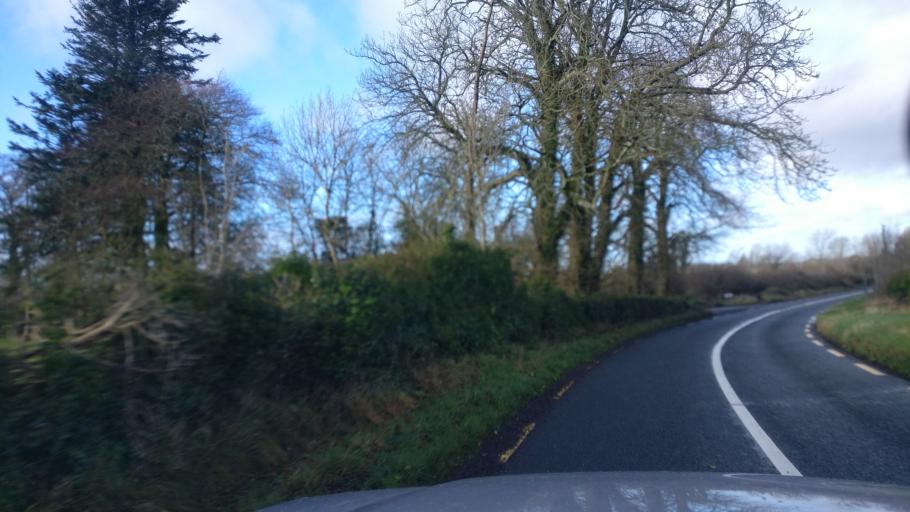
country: IE
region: Connaught
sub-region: County Galway
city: Athenry
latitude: 53.2556
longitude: -8.6786
